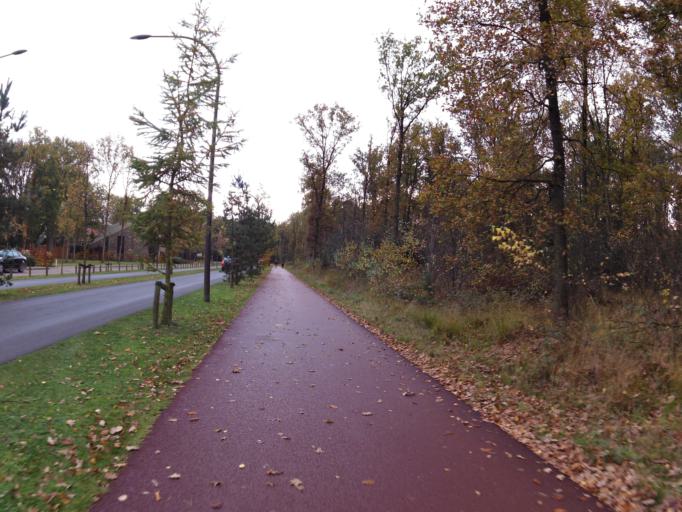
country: NL
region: North Brabant
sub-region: Gemeente Vught
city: Vught
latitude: 51.6643
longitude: 5.2810
